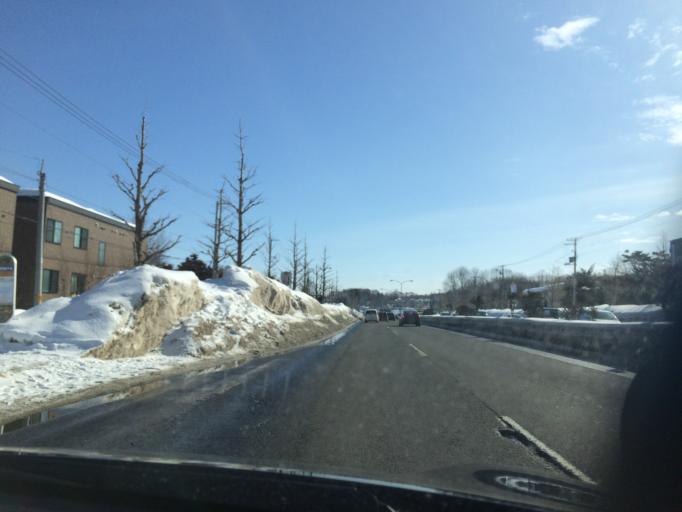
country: JP
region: Hokkaido
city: Kitahiroshima
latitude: 43.0207
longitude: 141.4751
